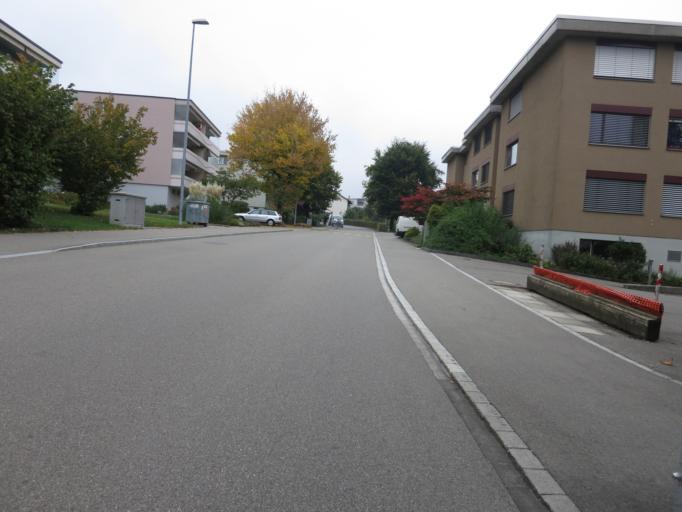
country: CH
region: Saint Gallen
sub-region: Wahlkreis See-Gaster
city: Rapperswil
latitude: 47.2390
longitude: 8.8211
